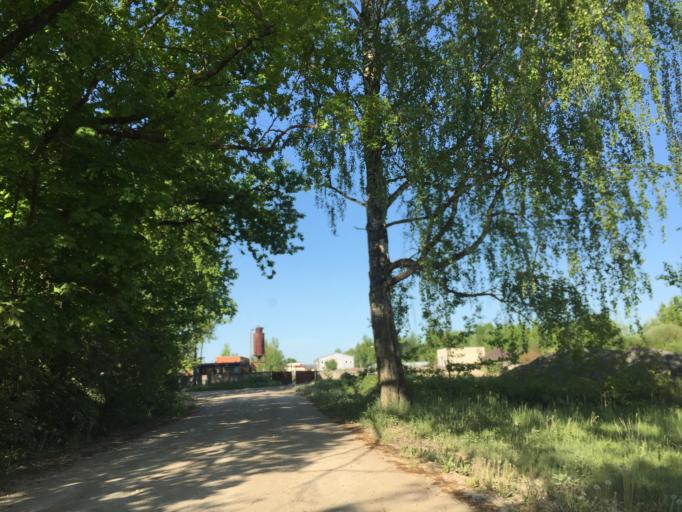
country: LV
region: Kekava
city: Kekava
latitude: 56.8206
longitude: 24.2372
